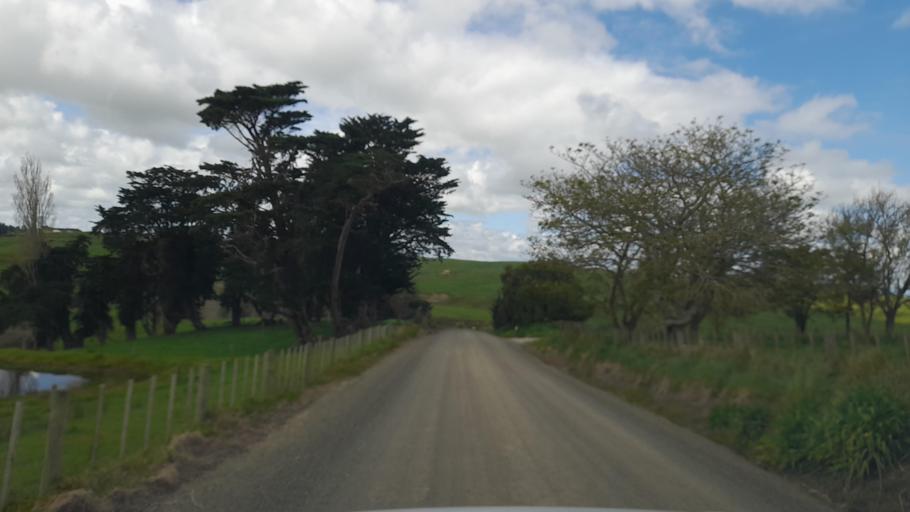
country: NZ
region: Auckland
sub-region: Auckland
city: Wellsford
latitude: -36.1906
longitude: 174.3257
